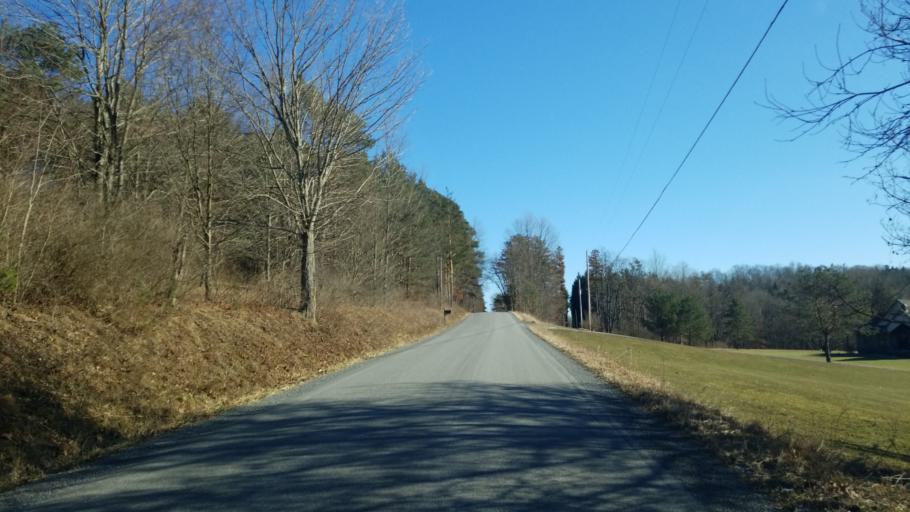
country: US
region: Pennsylvania
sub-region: Jefferson County
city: Sykesville
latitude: 41.0497
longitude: -78.7907
